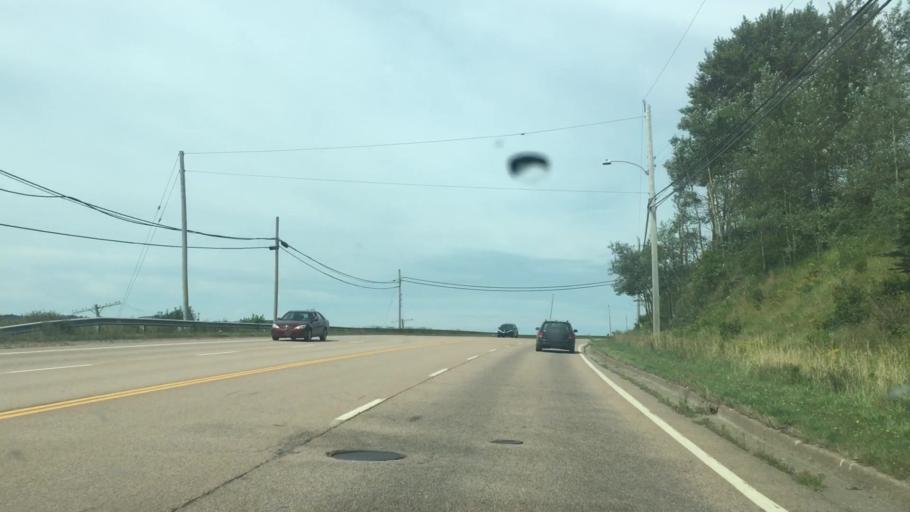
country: CA
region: Nova Scotia
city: Port Hawkesbury
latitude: 45.6262
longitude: -61.3711
